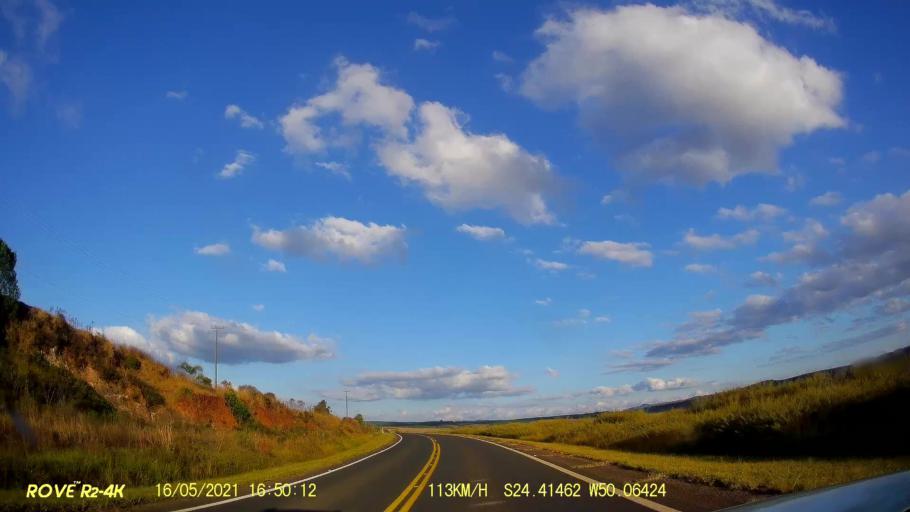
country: BR
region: Parana
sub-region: Pirai Do Sul
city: Pirai do Sul
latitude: -24.4157
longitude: -50.0626
